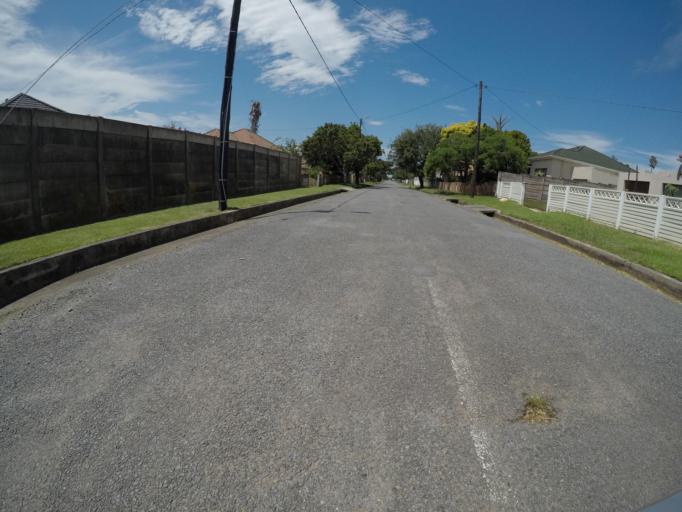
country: ZA
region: Eastern Cape
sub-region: Buffalo City Metropolitan Municipality
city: East London
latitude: -33.0336
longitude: 27.8563
